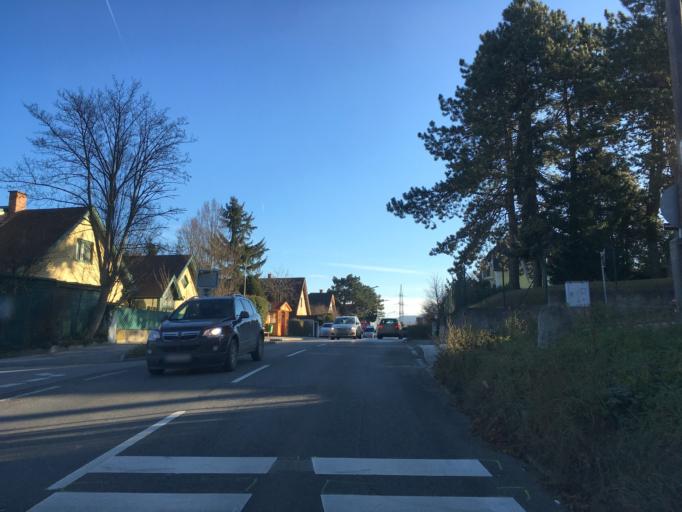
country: AT
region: Lower Austria
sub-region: Politischer Bezirk Wien-Umgebung
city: Klosterneuburg
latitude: 48.3222
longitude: 16.3061
